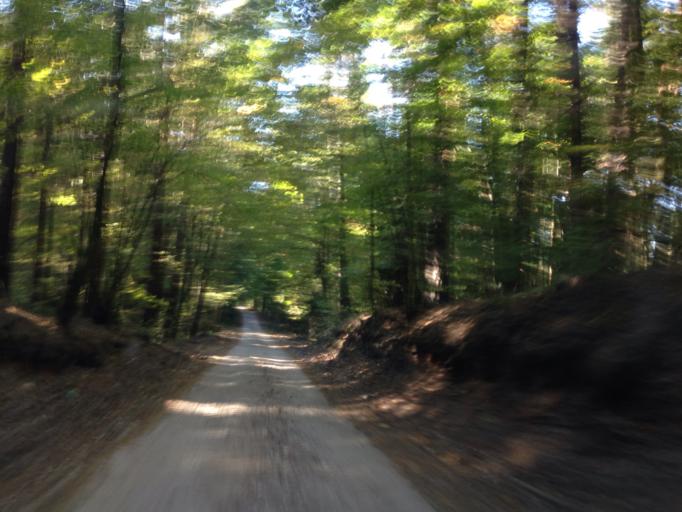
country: PL
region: Kujawsko-Pomorskie
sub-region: Powiat brodnicki
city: Gorzno
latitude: 53.2287
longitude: 19.7068
